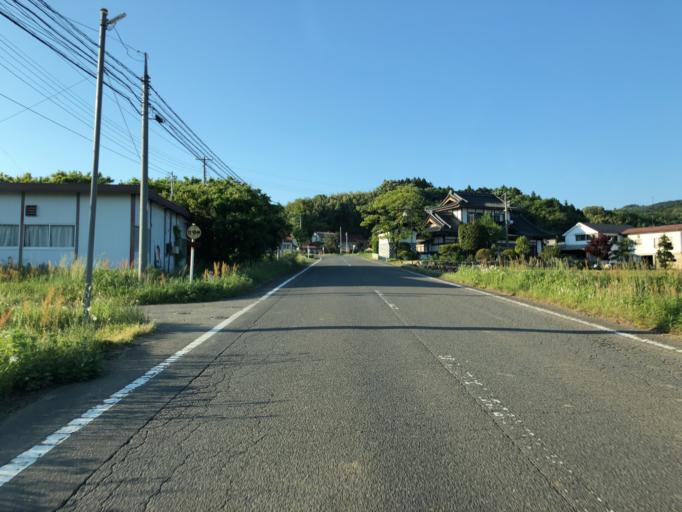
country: JP
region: Fukushima
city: Ishikawa
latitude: 36.9838
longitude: 140.4349
